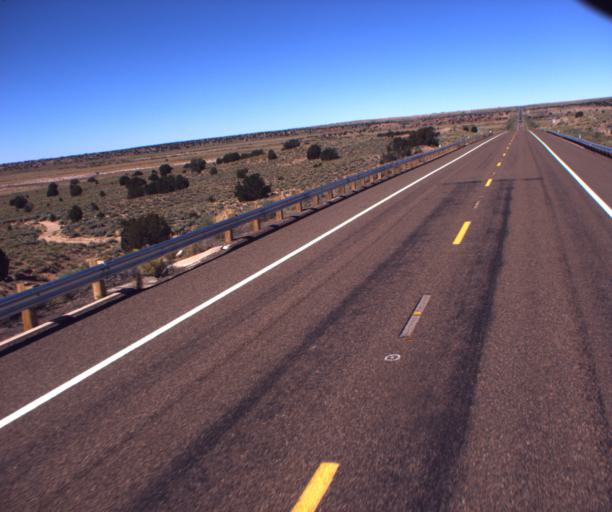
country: US
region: Arizona
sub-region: Apache County
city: Saint Johns
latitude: 34.6591
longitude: -109.7137
